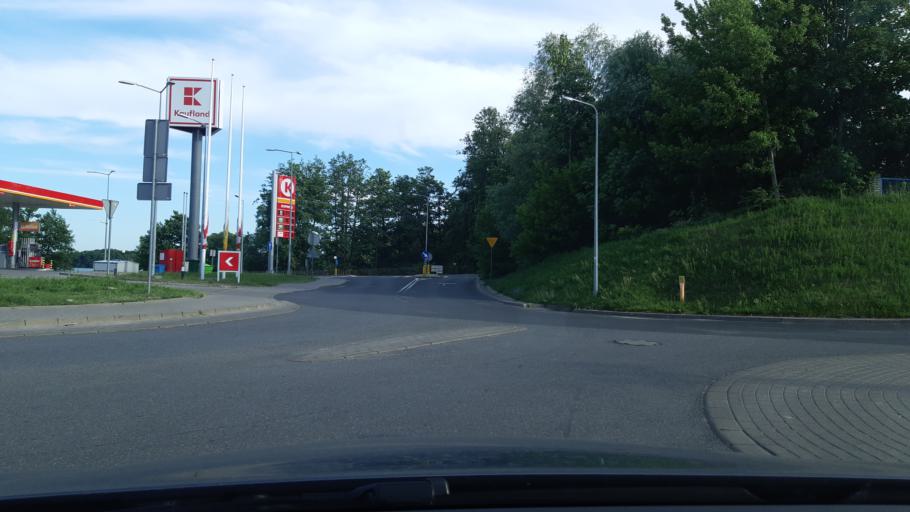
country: PL
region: Warmian-Masurian Voivodeship
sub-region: Powiat mragowski
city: Mragowo
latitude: 53.8780
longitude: 21.3065
